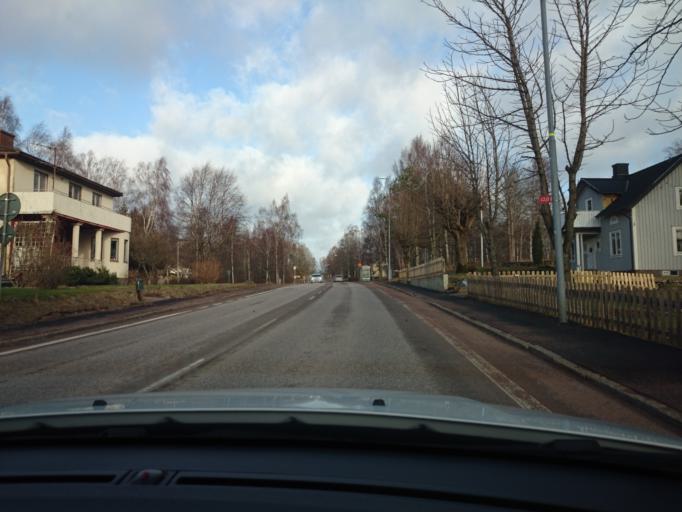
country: SE
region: Halland
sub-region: Hylte Kommun
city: Hyltebruk
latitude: 57.0100
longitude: 13.2428
